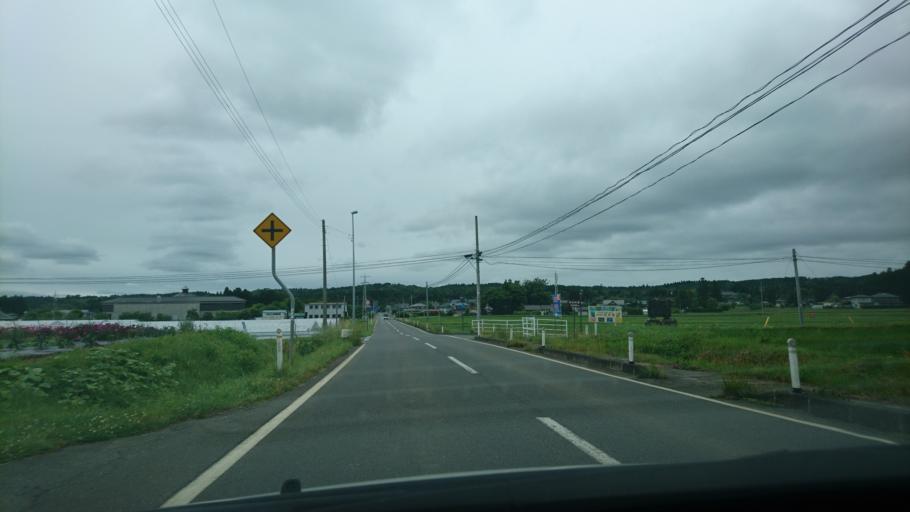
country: JP
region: Iwate
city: Ichinoseki
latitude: 38.9503
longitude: 141.0516
